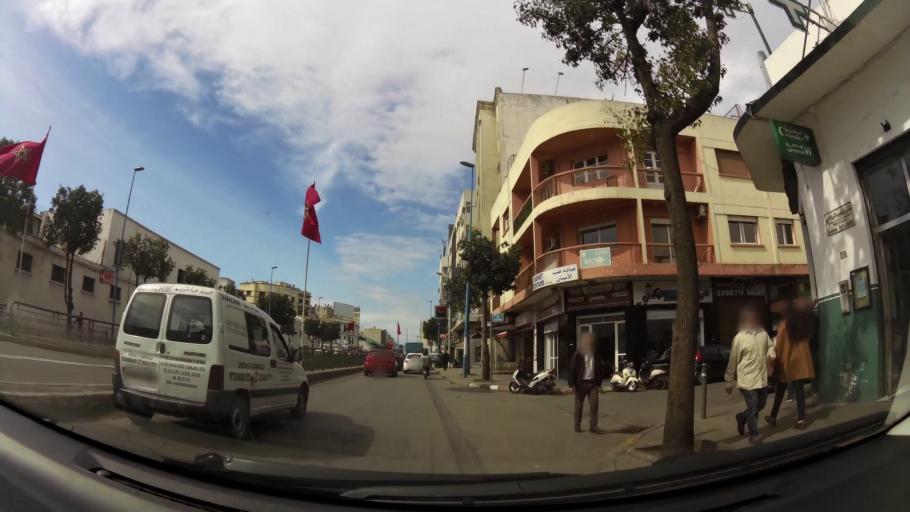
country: MA
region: Grand Casablanca
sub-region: Casablanca
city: Casablanca
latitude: 33.5808
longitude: -7.6345
